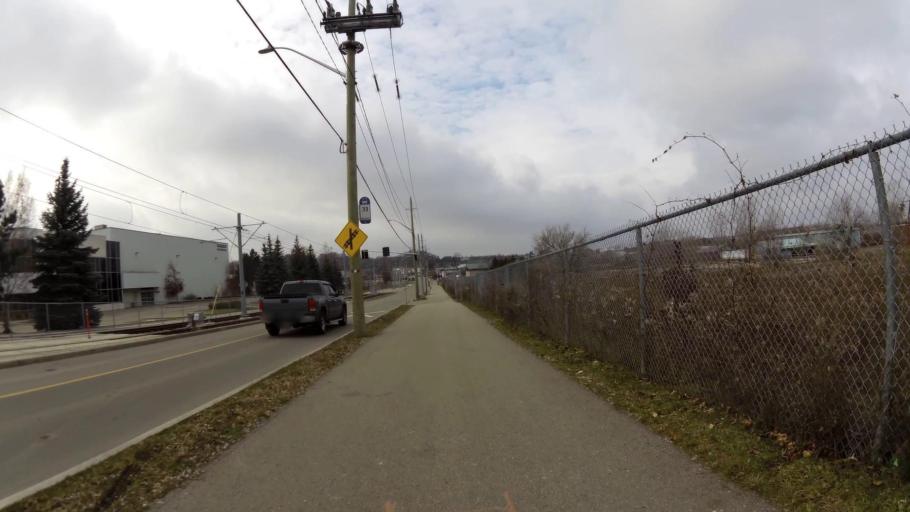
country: CA
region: Ontario
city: Kitchener
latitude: 43.4264
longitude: -80.4666
